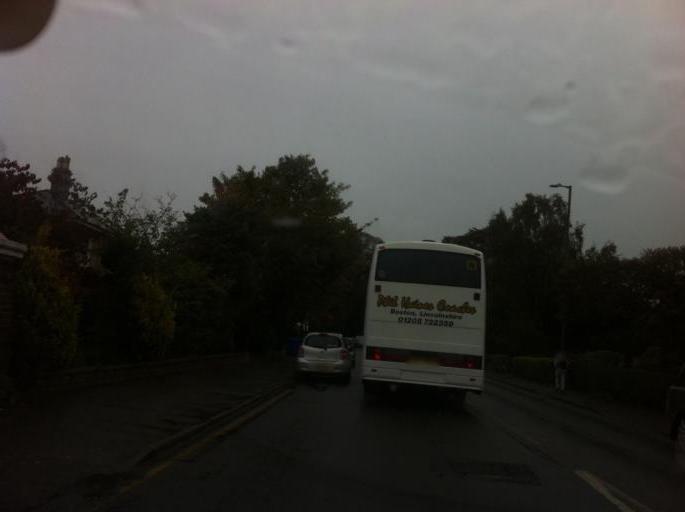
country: GB
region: England
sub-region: Lincolnshire
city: Boston
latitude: 52.9863
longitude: -0.0105
